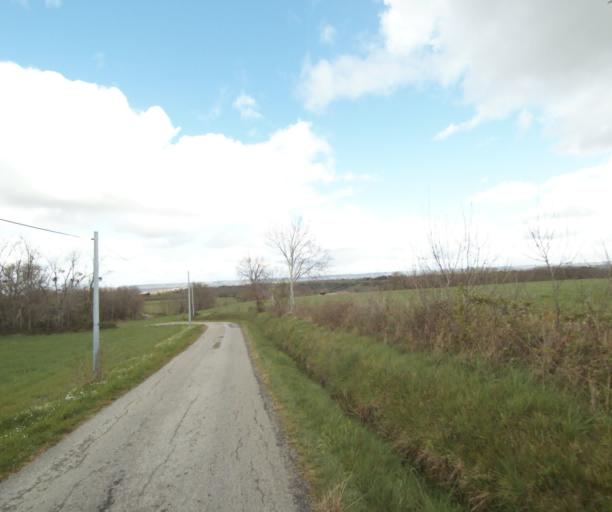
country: FR
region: Midi-Pyrenees
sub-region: Departement de l'Ariege
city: Saverdun
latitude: 43.2054
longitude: 1.5663
